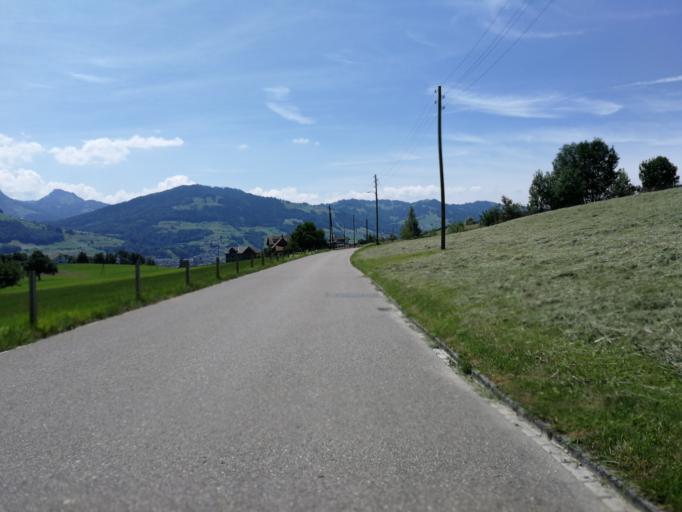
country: CH
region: Schwyz
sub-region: Bezirk March
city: Tuggen
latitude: 47.2001
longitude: 8.9239
